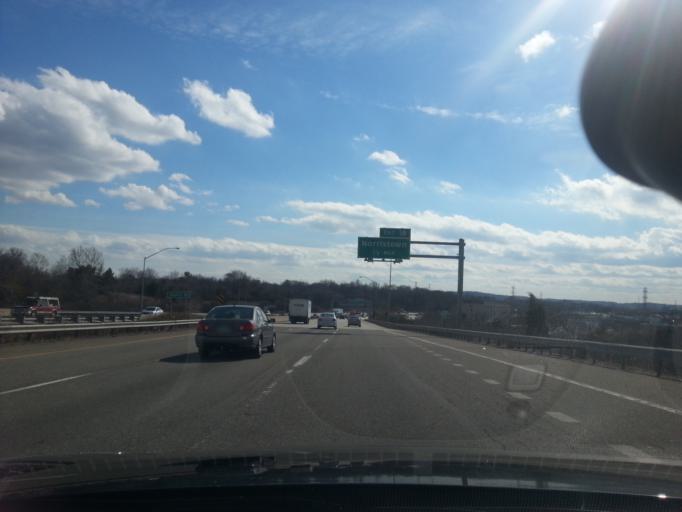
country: US
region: Pennsylvania
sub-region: Montgomery County
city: Plymouth Meeting
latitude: 40.1046
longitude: -75.2899
